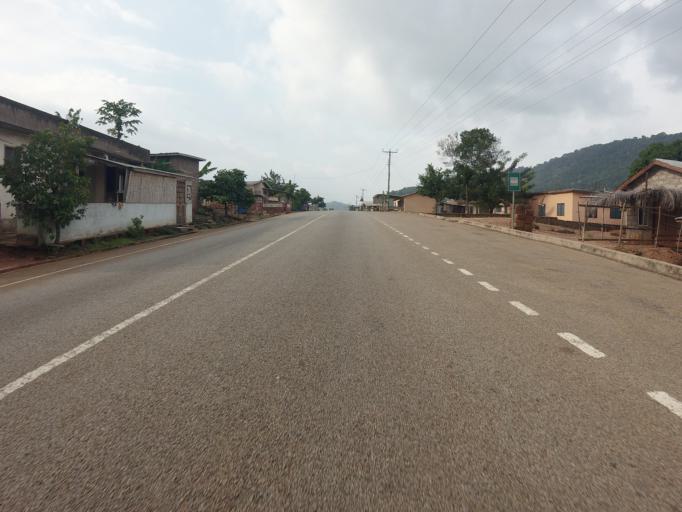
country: GH
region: Volta
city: Ho
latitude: 6.6660
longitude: 0.4744
